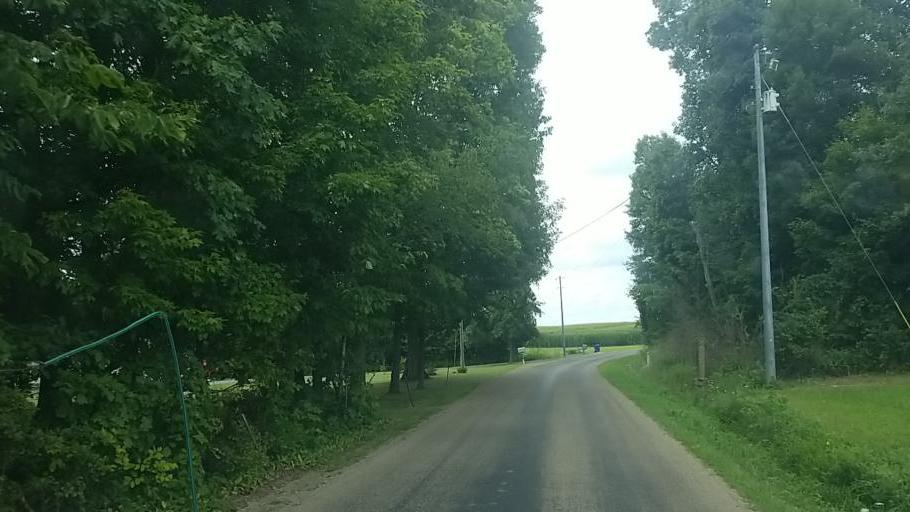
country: US
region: Ohio
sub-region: Knox County
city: Gambier
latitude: 40.3326
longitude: -82.4310
